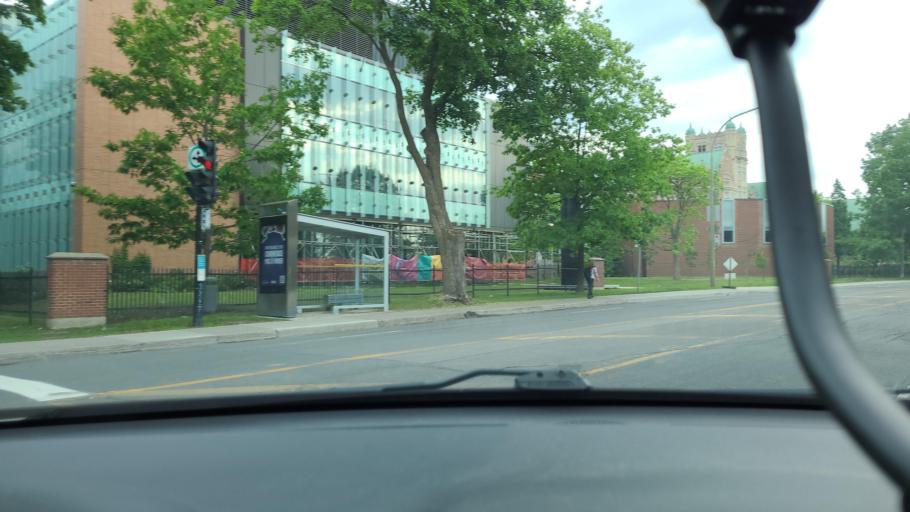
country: CA
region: Quebec
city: Montreal-Ouest
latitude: 45.4566
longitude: -73.6401
